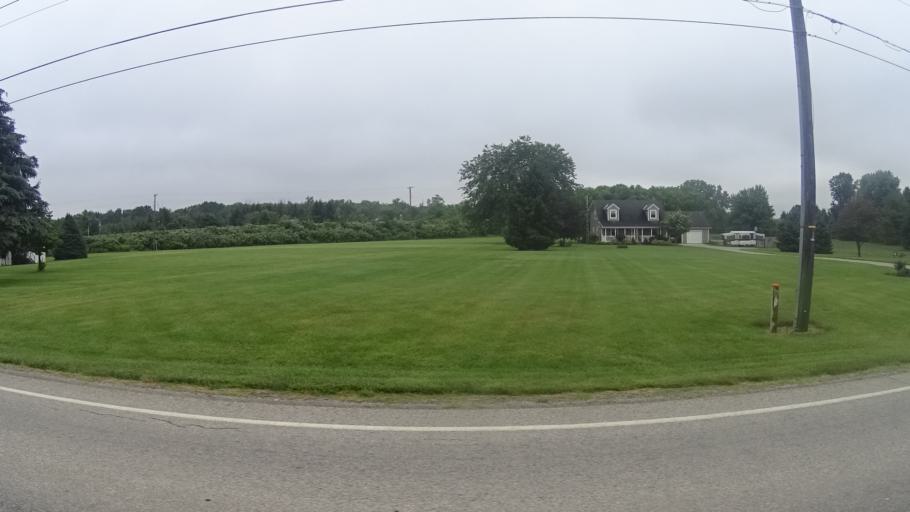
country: US
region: Ohio
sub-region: Erie County
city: Milan
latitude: 41.3361
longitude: -82.5890
